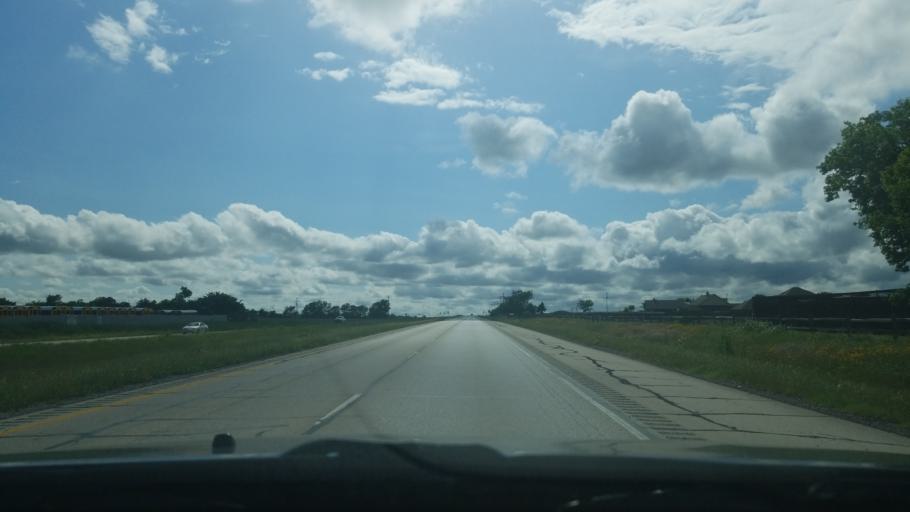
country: US
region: Texas
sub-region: Denton County
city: Ponder
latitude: 33.2502
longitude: -97.4235
